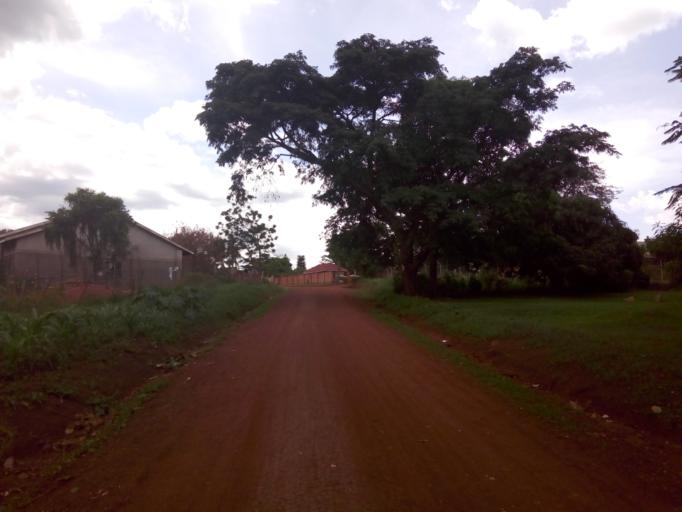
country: UG
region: Western Region
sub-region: Masindi District
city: Masindi
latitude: 1.6867
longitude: 31.7208
